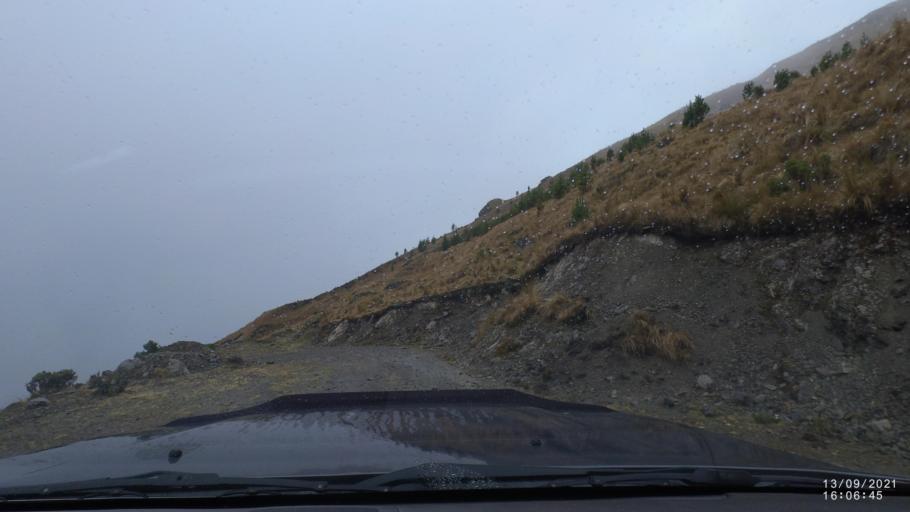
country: BO
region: Cochabamba
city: Colomi
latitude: -17.2810
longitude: -65.7096
